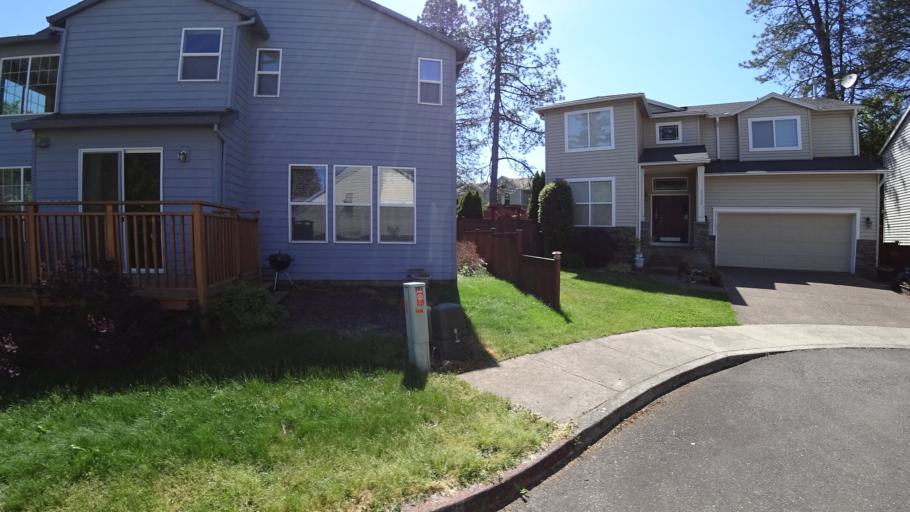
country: US
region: Oregon
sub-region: Washington County
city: Metzger
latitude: 45.4482
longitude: -122.7221
